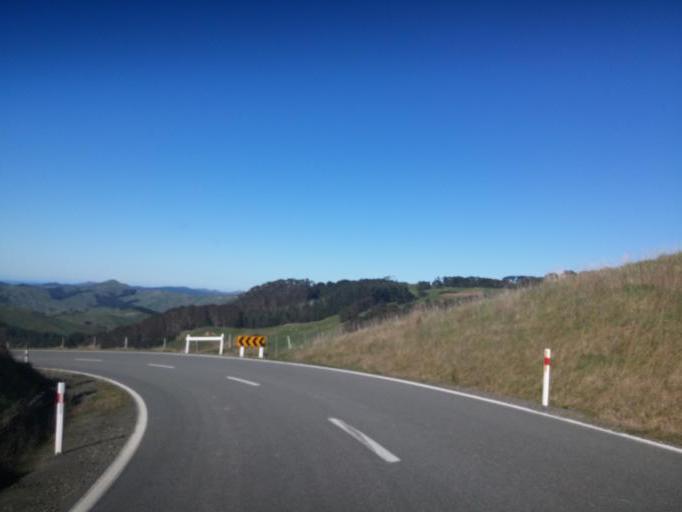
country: NZ
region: Wellington
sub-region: South Wairarapa District
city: Waipawa
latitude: -41.3601
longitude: 175.4904
